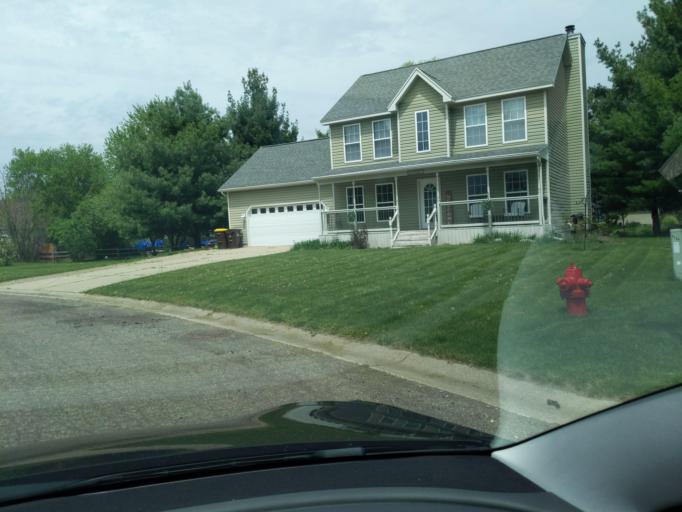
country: US
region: Michigan
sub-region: Ingham County
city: Holt
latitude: 42.6537
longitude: -84.5636
